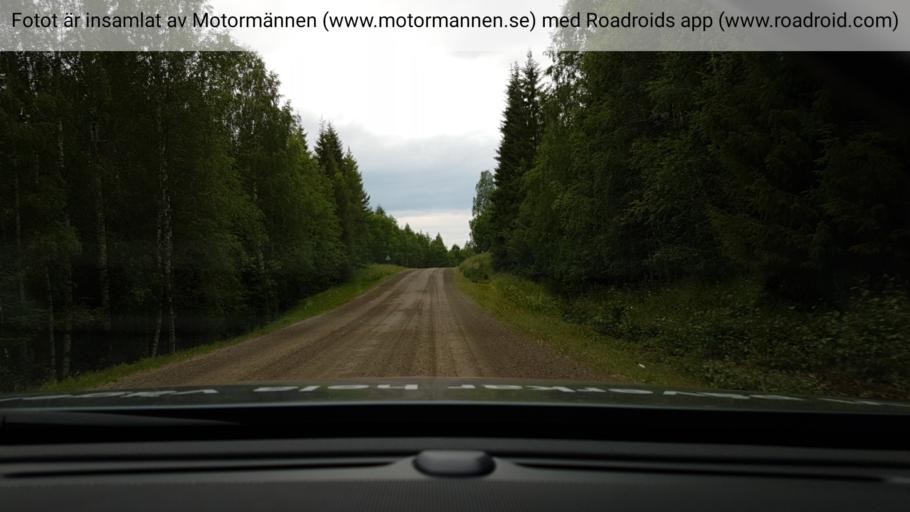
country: SE
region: Vaesterbotten
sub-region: Vannas Kommun
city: Vannasby
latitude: 64.0916
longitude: 20.0270
